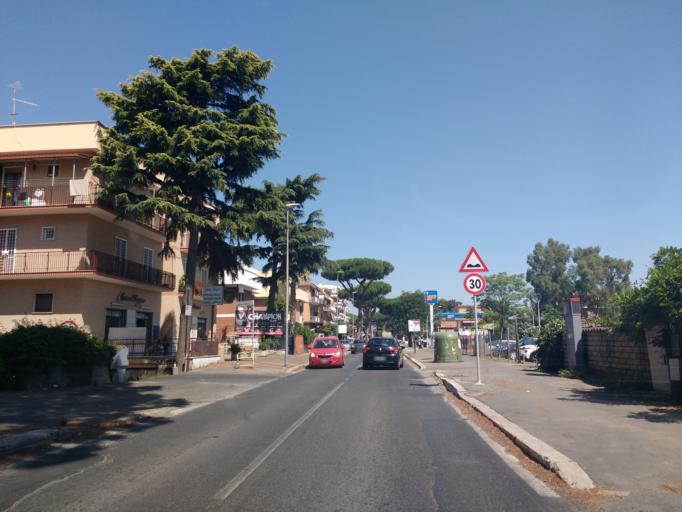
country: IT
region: Latium
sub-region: Citta metropolitana di Roma Capitale
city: Acilia-Castel Fusano-Ostia Antica
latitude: 41.7795
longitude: 12.3675
